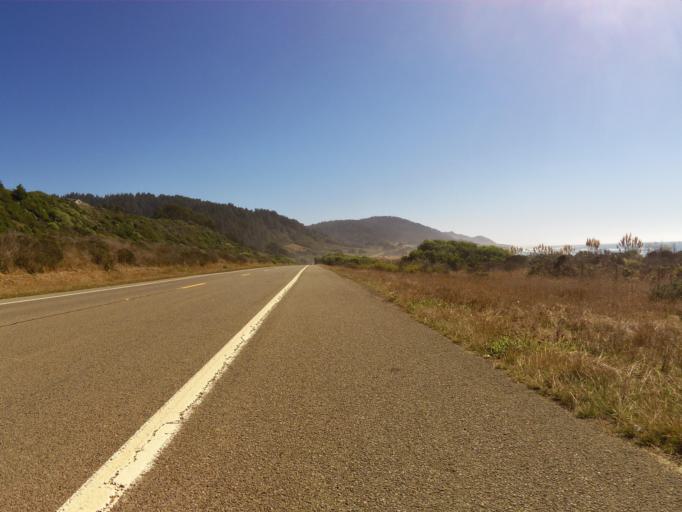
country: US
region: California
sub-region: Mendocino County
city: Fort Bragg
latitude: 39.6648
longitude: -123.7879
